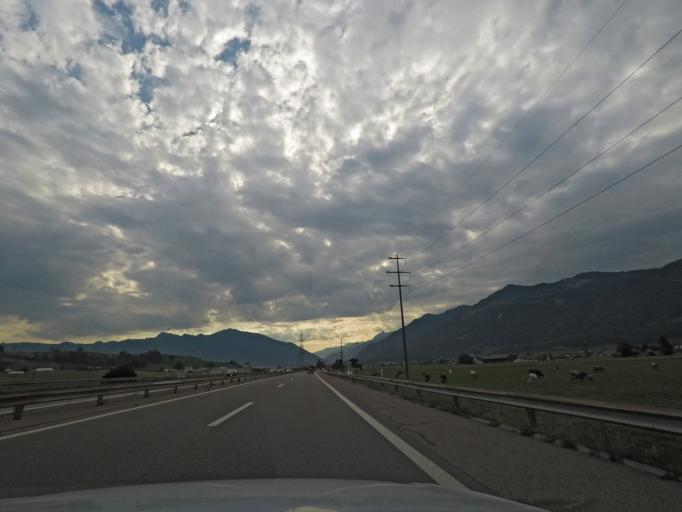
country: CH
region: Schwyz
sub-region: Bezirk March
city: Schubelbach
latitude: 47.1879
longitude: 8.9199
